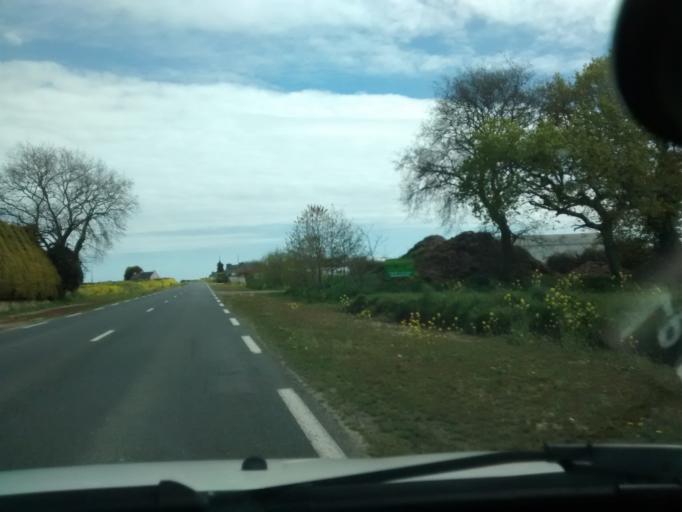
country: FR
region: Brittany
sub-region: Departement des Cotes-d'Armor
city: Pleumeur-Gautier
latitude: 48.7809
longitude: -3.1685
